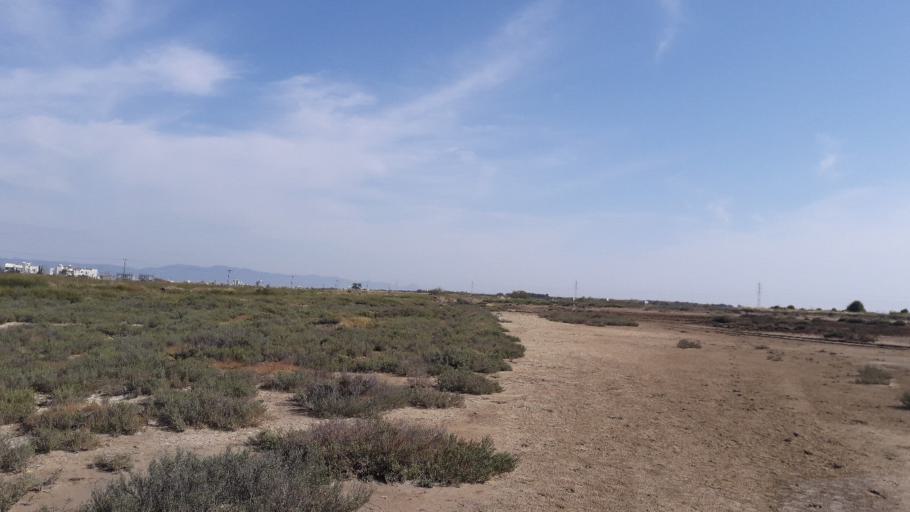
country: CY
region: Ammochostos
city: Famagusta
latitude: 35.1609
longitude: 33.8920
